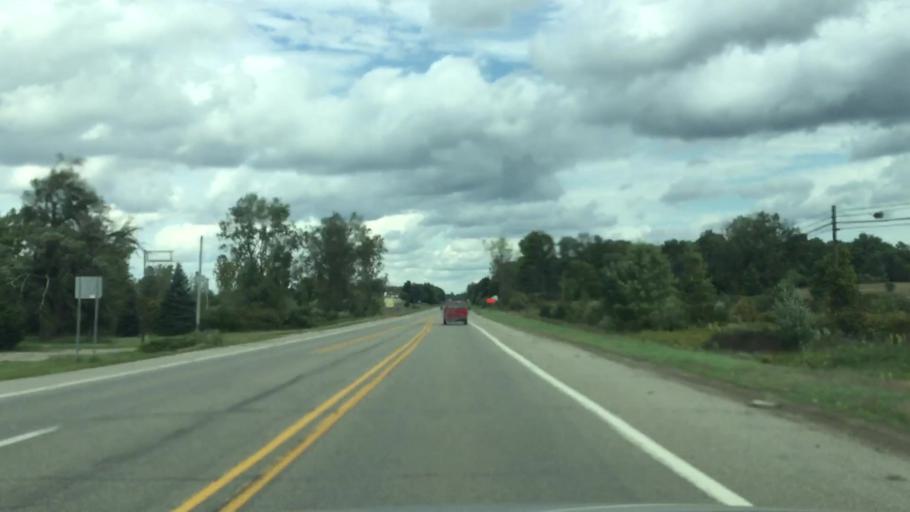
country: US
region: Michigan
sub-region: Shiawassee County
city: Owosso
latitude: 42.9591
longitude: -84.2062
